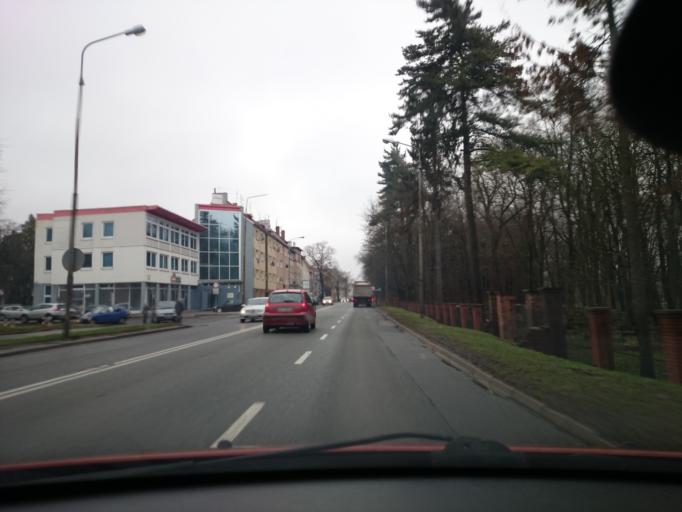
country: PL
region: Opole Voivodeship
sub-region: Powiat opolski
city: Opole
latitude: 50.6749
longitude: 17.9081
